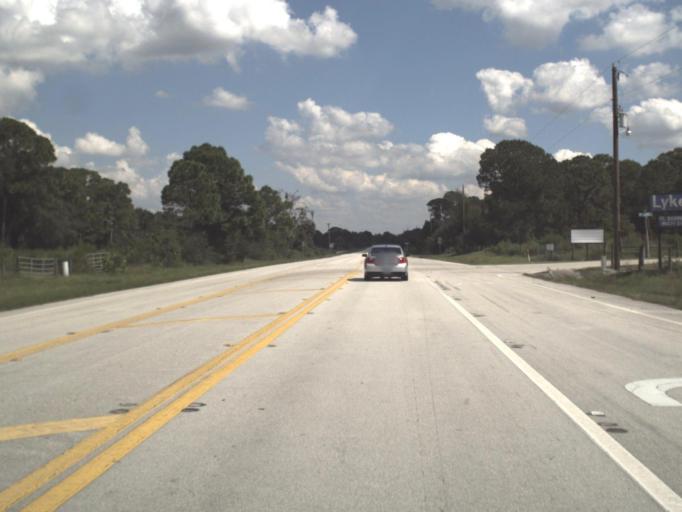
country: US
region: Florida
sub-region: Highlands County
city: Lake Placid
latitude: 27.3814
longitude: -81.1184
